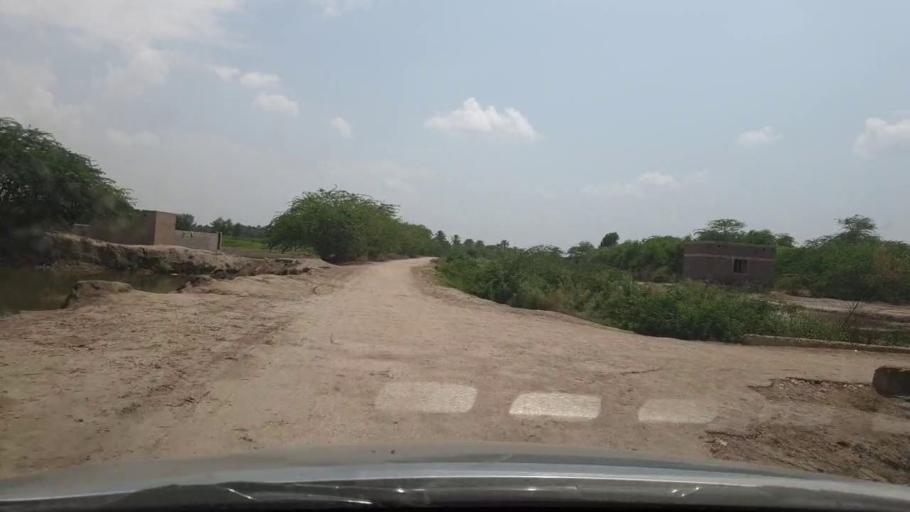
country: PK
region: Sindh
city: Kot Diji
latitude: 27.3823
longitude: 68.7142
